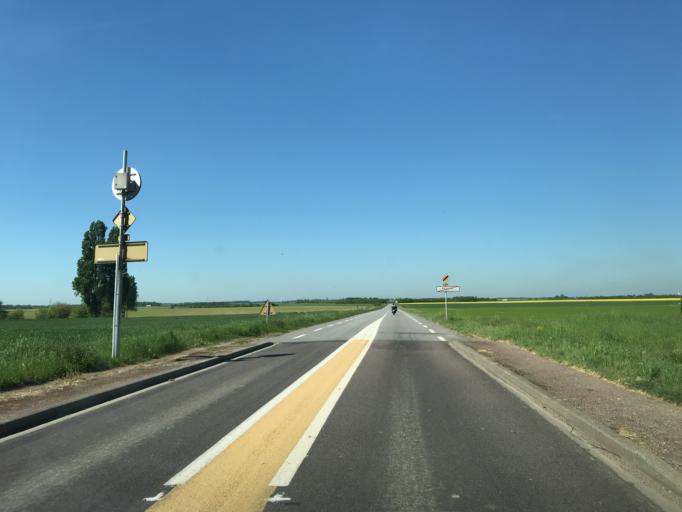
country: FR
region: Haute-Normandie
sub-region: Departement de l'Eure
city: La Madeleine-de-Nonancourt
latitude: 48.8907
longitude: 1.1915
